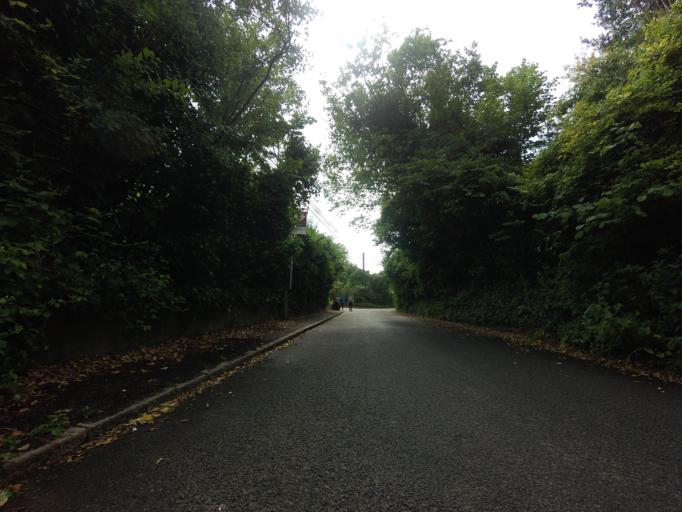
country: GB
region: England
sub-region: Kent
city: Halstead
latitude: 51.3542
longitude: 0.1375
